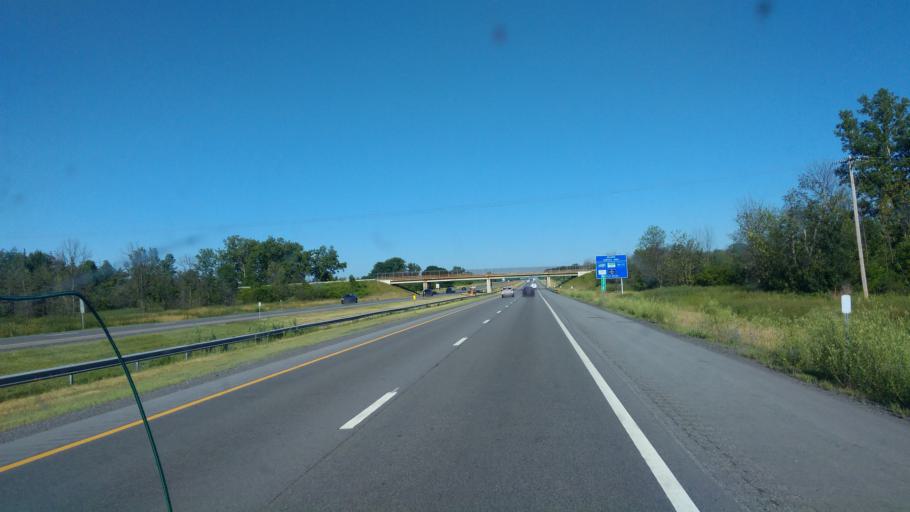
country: US
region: New York
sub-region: Livingston County
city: Caledonia
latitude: 43.0301
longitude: -77.8740
